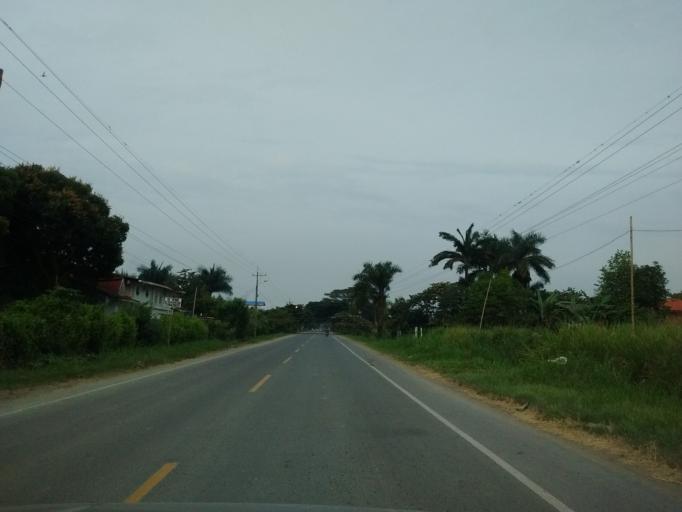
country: CO
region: Cauca
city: Puerto Tejada
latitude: 3.1831
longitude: -76.4515
